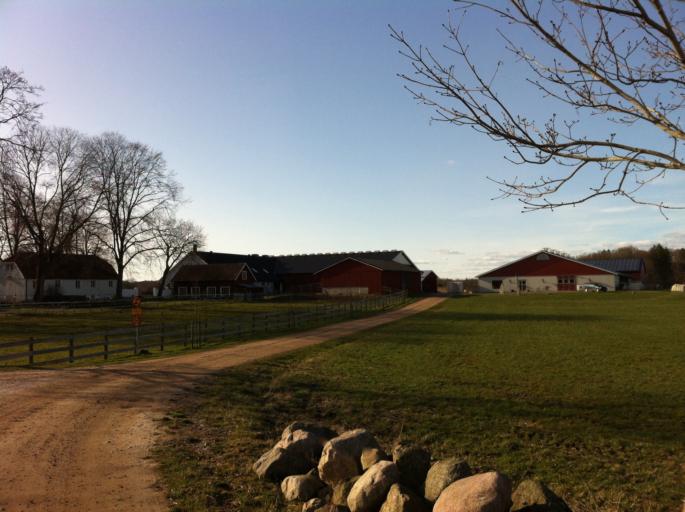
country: SE
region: Skane
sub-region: Hassleholms Kommun
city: Sosdala
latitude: 56.0614
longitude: 13.6924
